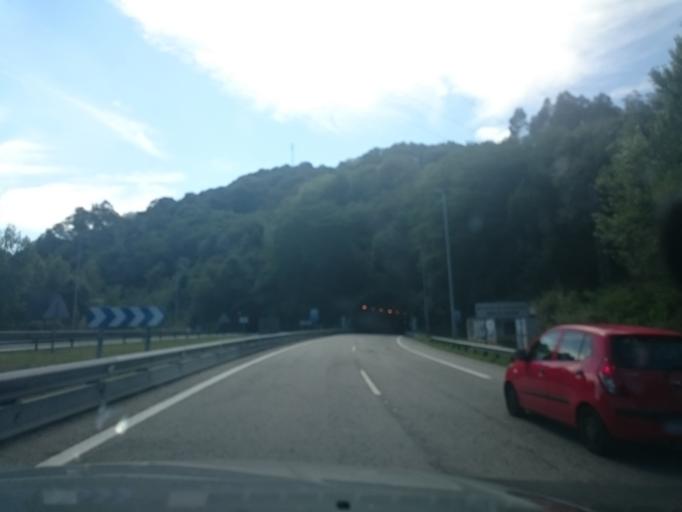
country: ES
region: Asturias
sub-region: Province of Asturias
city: Mieres
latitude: 43.2955
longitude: -5.8143
